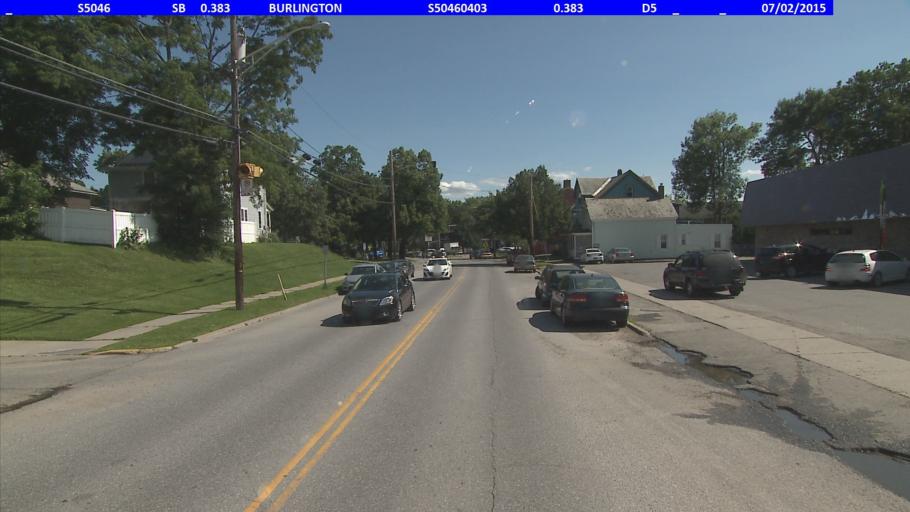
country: US
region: Vermont
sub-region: Chittenden County
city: Burlington
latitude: 44.4724
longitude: -73.2138
